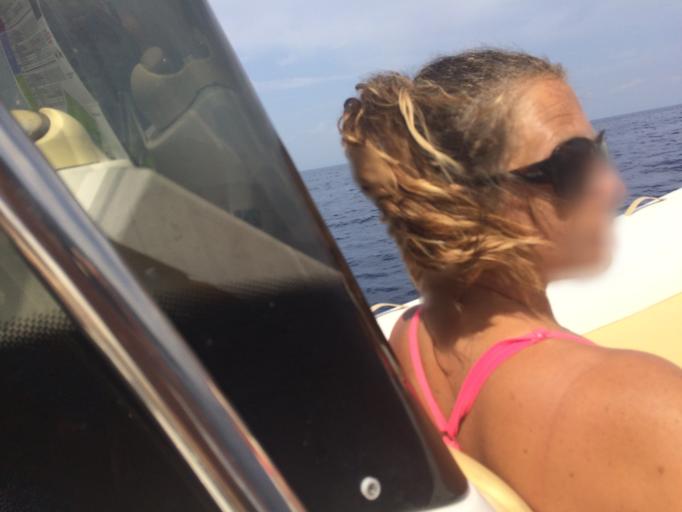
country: IT
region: Tuscany
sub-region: Provincia di Livorno
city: Capraia Isola
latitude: 43.0468
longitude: 9.7933
